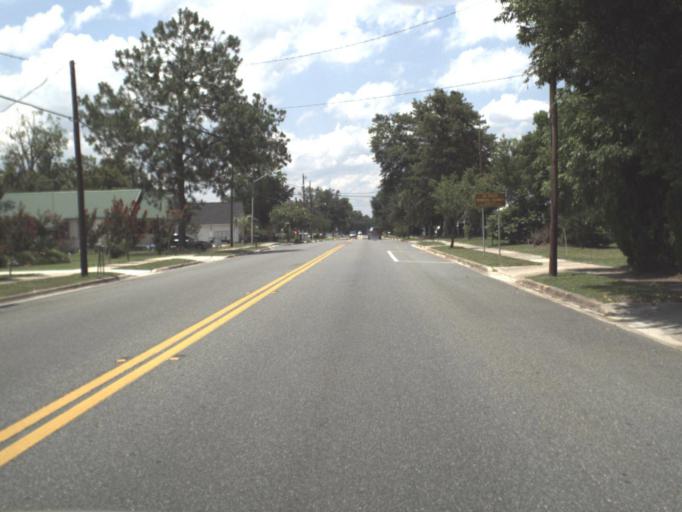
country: US
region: Florida
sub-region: Baker County
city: Macclenny
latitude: 30.2852
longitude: -82.1244
